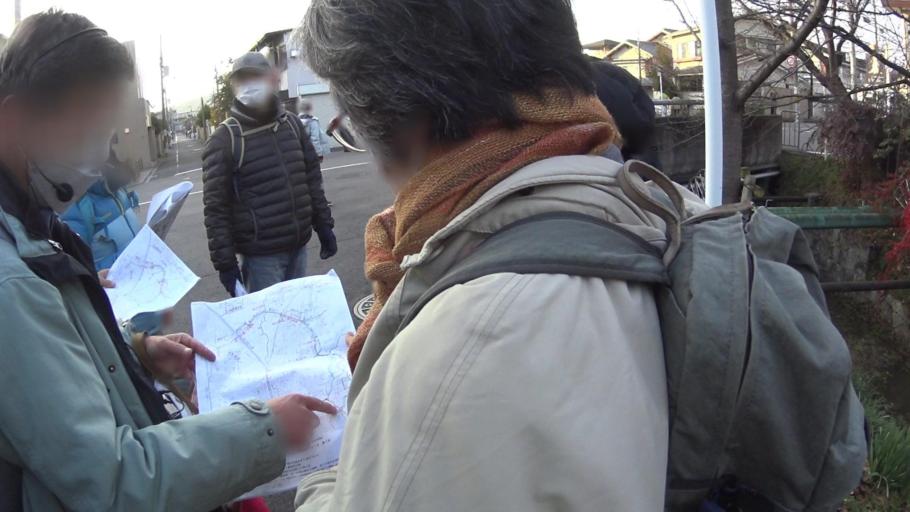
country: JP
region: Kyoto
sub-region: Kyoto-shi
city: Kamigyo-ku
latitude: 35.0466
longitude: 135.7766
